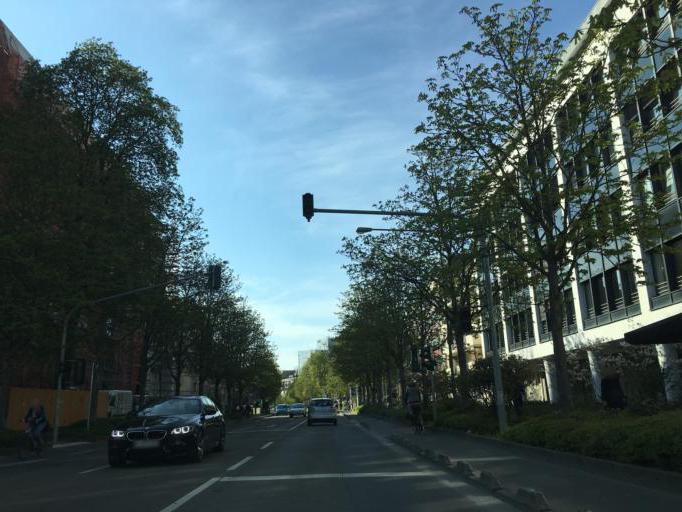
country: DE
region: Hesse
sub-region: Regierungsbezirk Darmstadt
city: Frankfurt am Main
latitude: 50.1185
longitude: 8.6621
